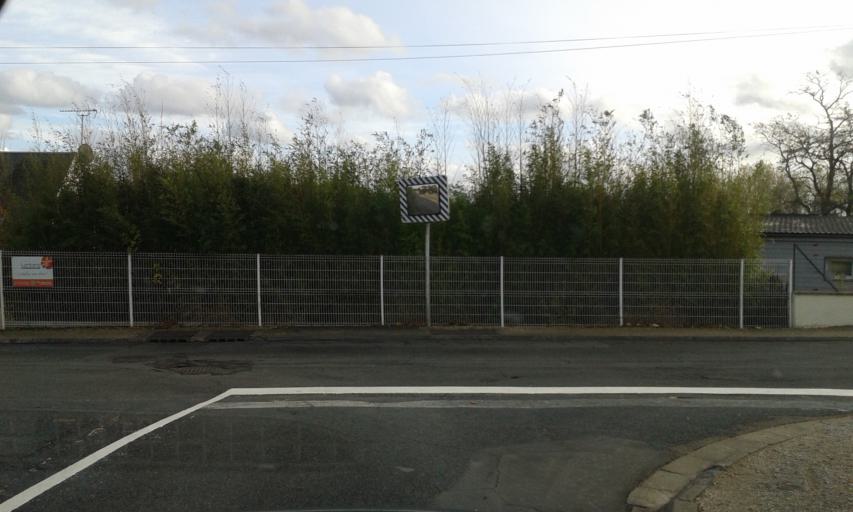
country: FR
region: Centre
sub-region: Departement du Loiret
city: Tavers
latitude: 47.7601
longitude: 1.6196
